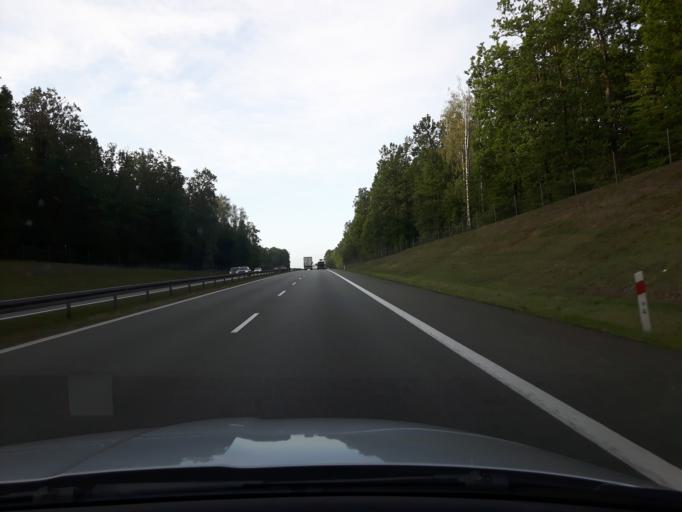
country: PL
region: Masovian Voivodeship
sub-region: Powiat bialobrzeski
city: Bialobrzegi
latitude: 51.6393
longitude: 20.9721
